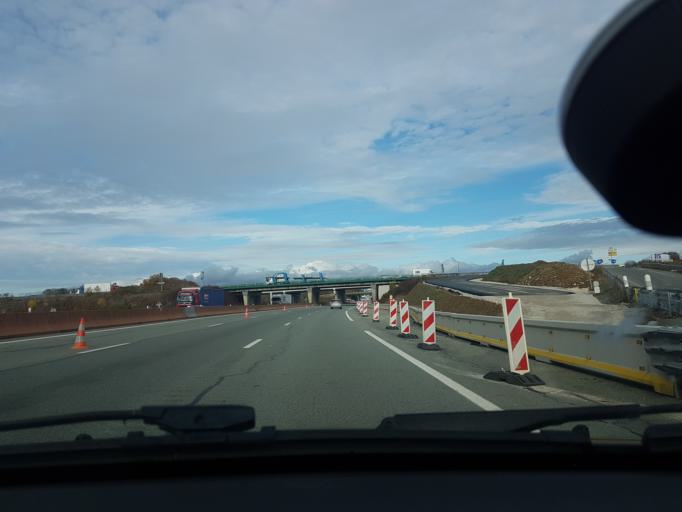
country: FR
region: Franche-Comte
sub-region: Territoire de Belfort
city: Andelnans
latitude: 47.5838
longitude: 6.8560
